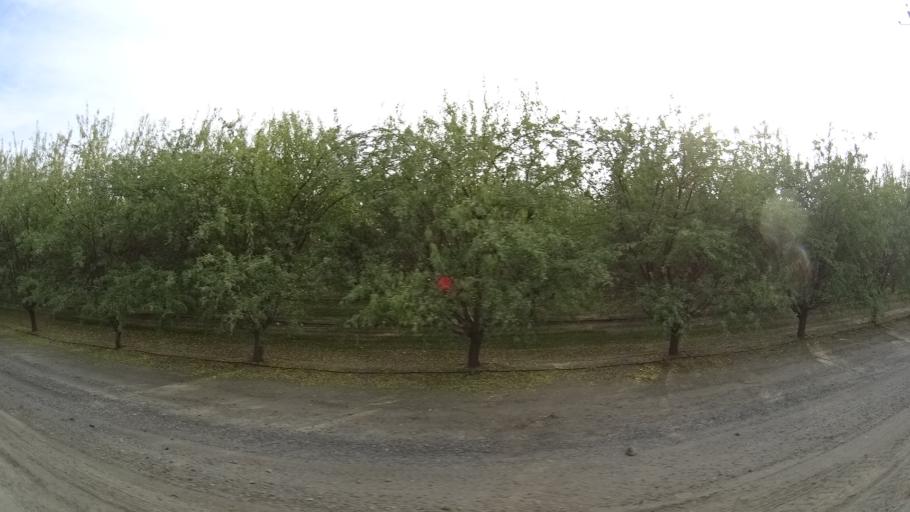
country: US
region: California
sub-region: Kern County
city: Rosedale
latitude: 35.2672
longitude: -119.1322
